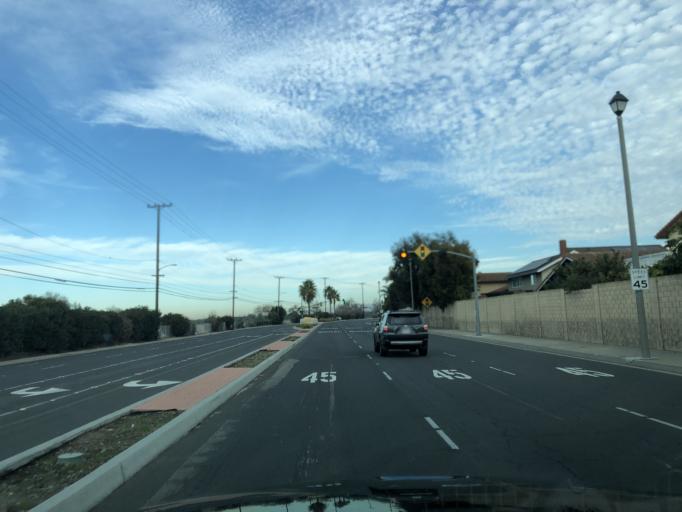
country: US
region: California
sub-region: Orange County
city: Westminster
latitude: 33.7506
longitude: -118.0420
